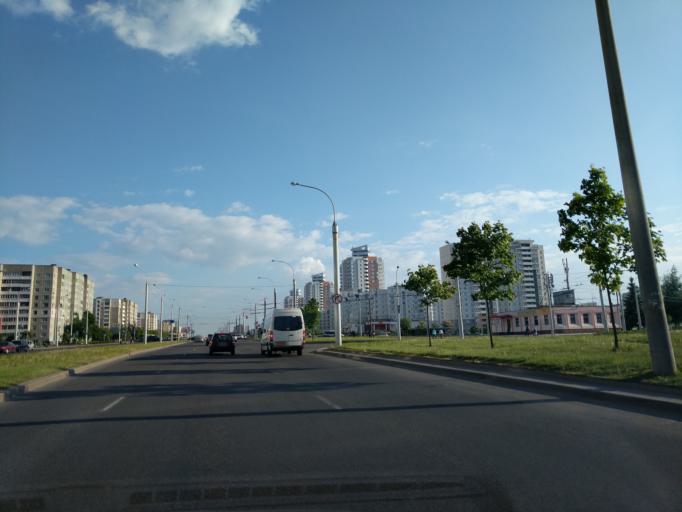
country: BY
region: Minsk
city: Zhdanovichy
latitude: 53.9177
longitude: 27.4370
